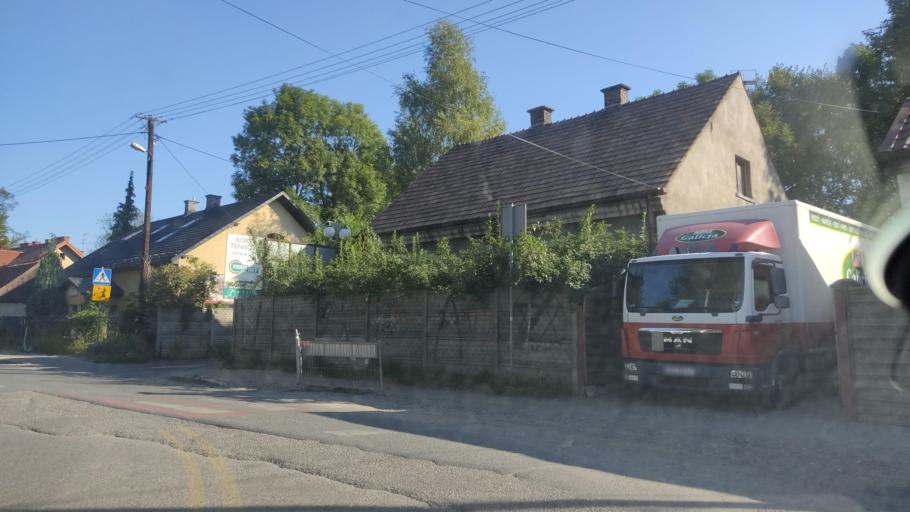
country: PL
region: Lesser Poland Voivodeship
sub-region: Powiat krakowski
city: Zielonki
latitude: 50.0952
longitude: 19.9351
